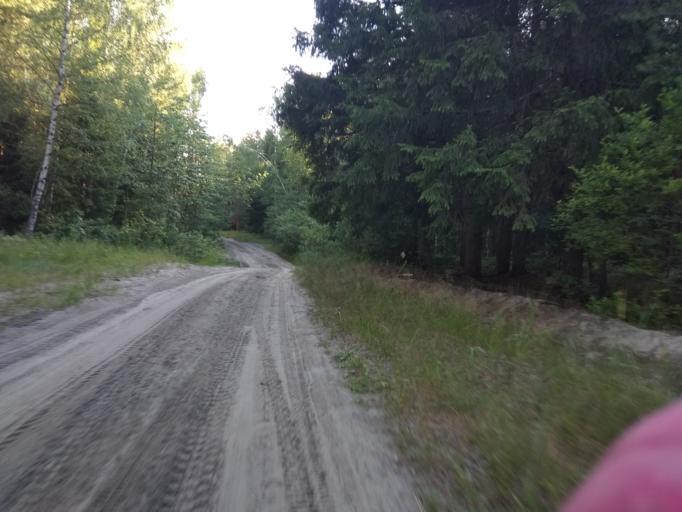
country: RU
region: Moskovskaya
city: Misheronskiy
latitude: 55.7315
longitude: 39.7638
